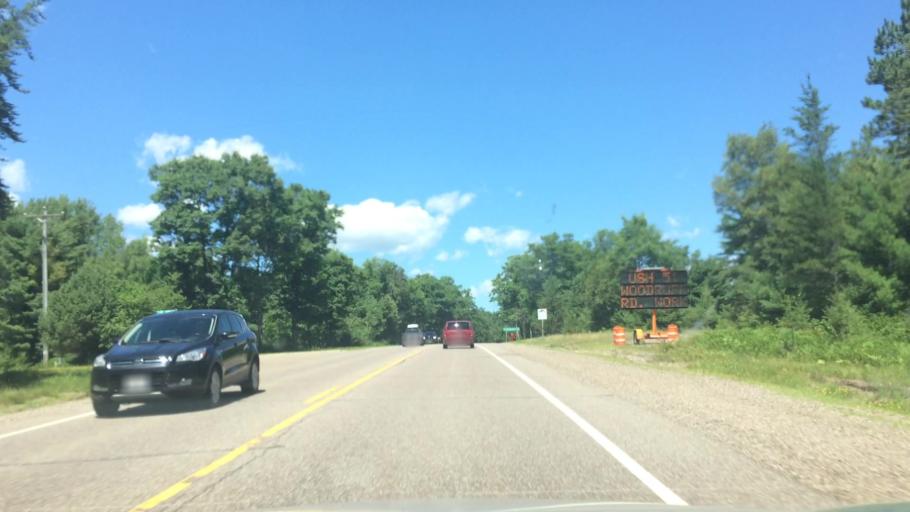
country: US
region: Wisconsin
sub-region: Vilas County
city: Lac du Flambeau
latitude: 45.7780
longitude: -89.7150
